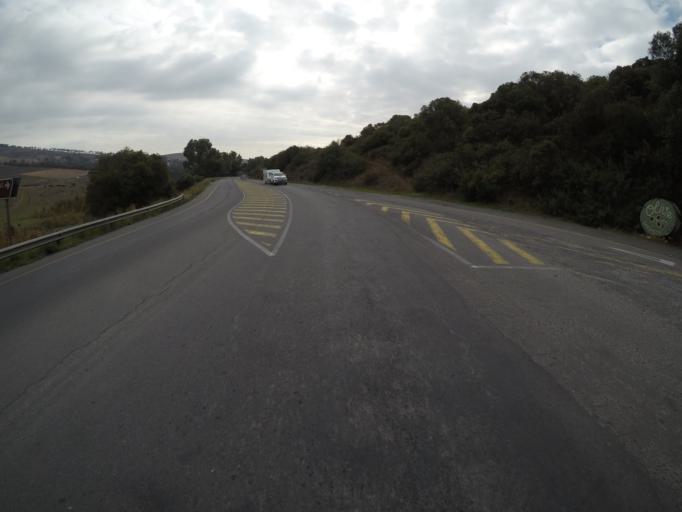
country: ZA
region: Western Cape
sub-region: City of Cape Town
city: Sunset Beach
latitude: -33.8258
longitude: 18.5891
